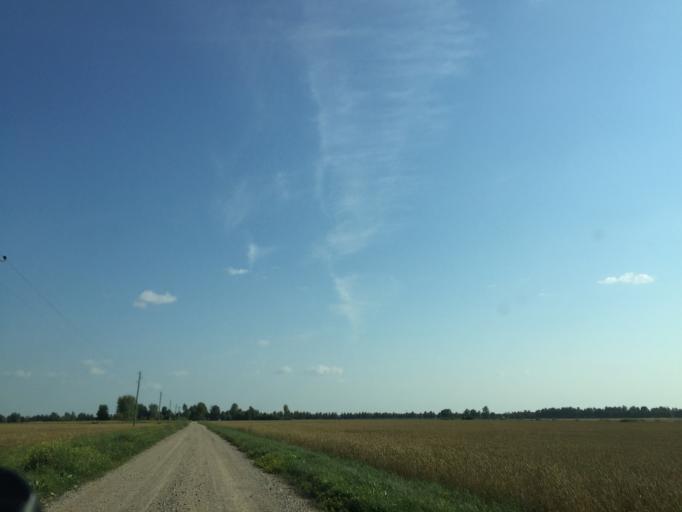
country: LV
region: Jelgava
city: Jelgava
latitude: 56.4598
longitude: 23.6807
